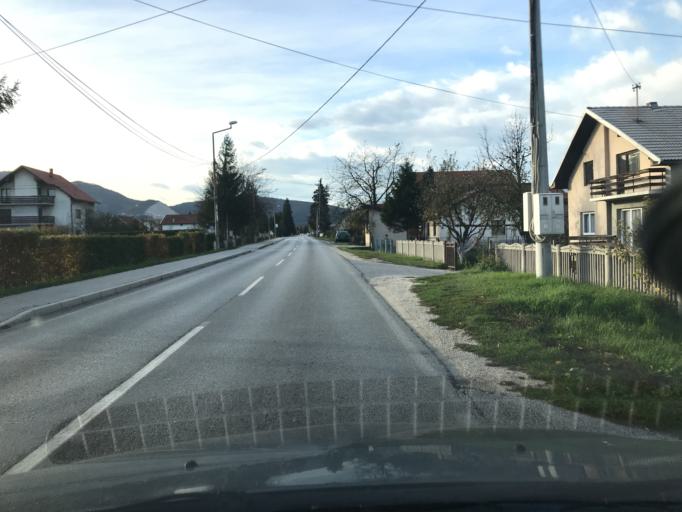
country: BA
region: Federation of Bosnia and Herzegovina
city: Vitez
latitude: 44.1619
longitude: 17.7808
